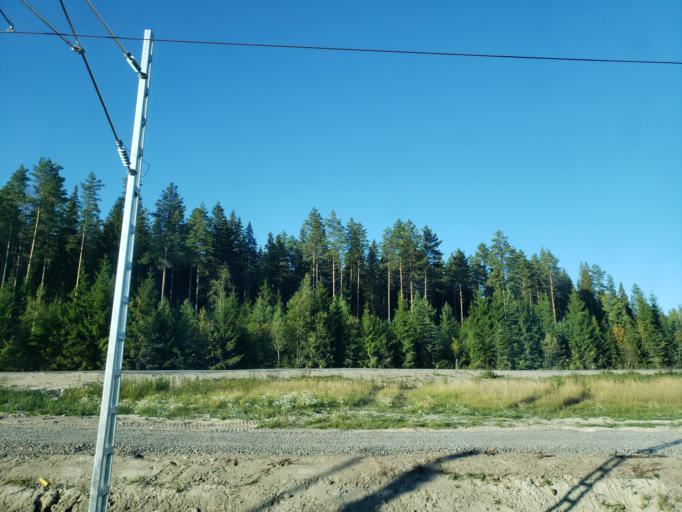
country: FI
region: South Karelia
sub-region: Lappeenranta
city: Nuijamaa
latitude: 60.8577
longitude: 28.3294
